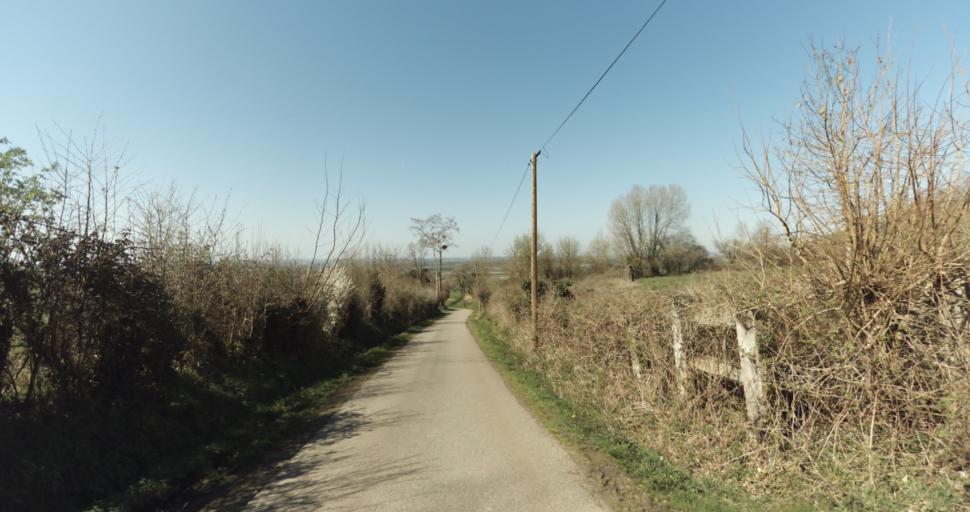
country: FR
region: Lower Normandy
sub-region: Departement du Calvados
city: Saint-Pierre-sur-Dives
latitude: 48.9902
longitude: 0.0445
